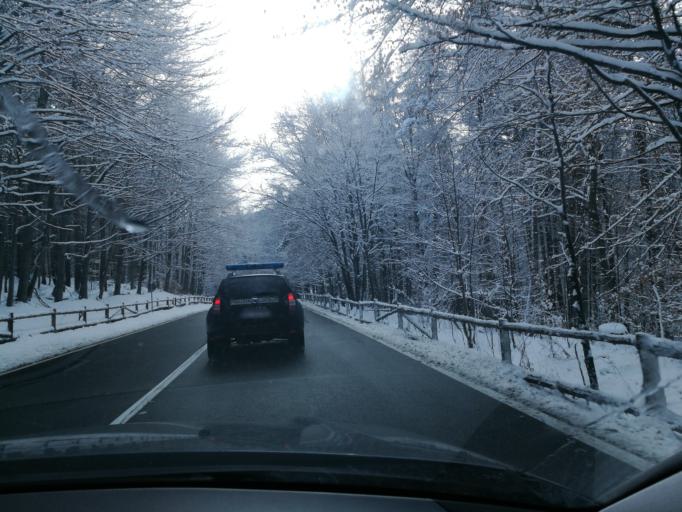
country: RO
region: Brasov
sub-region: Comuna Ghimbav
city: Ghimbav
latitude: 45.6183
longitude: 25.5442
